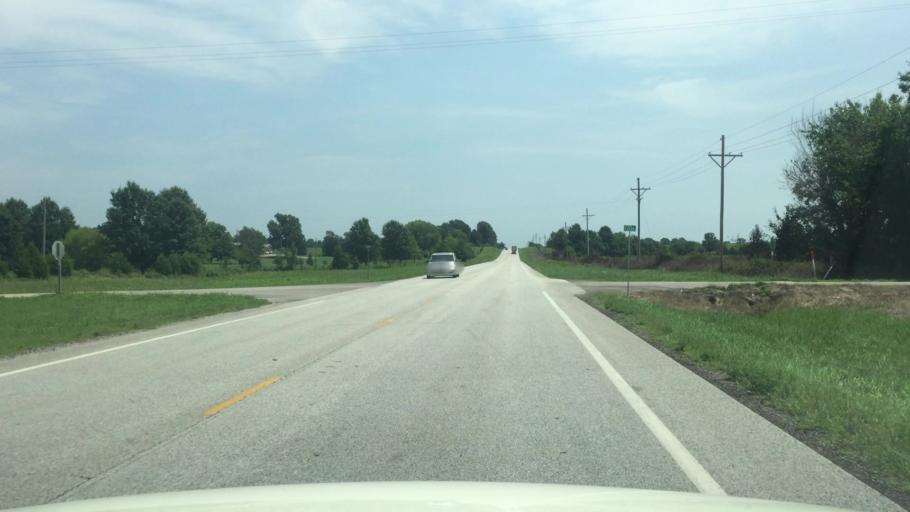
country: US
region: Kansas
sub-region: Cherokee County
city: Columbus
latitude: 37.1780
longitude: -94.7961
